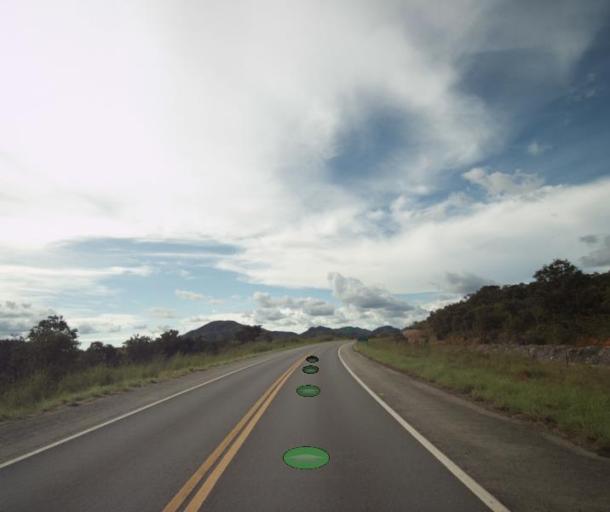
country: BR
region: Goias
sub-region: Barro Alto
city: Barro Alto
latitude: -15.1062
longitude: -48.7497
